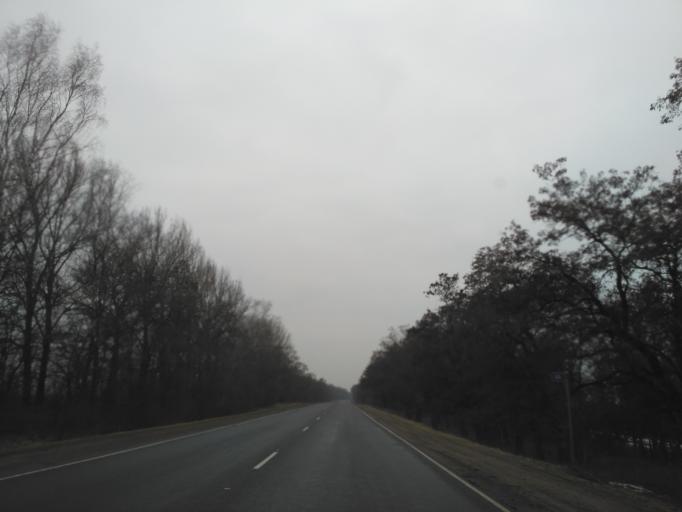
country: BY
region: Brest
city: Baranovichi
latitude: 53.1871
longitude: 26.0772
